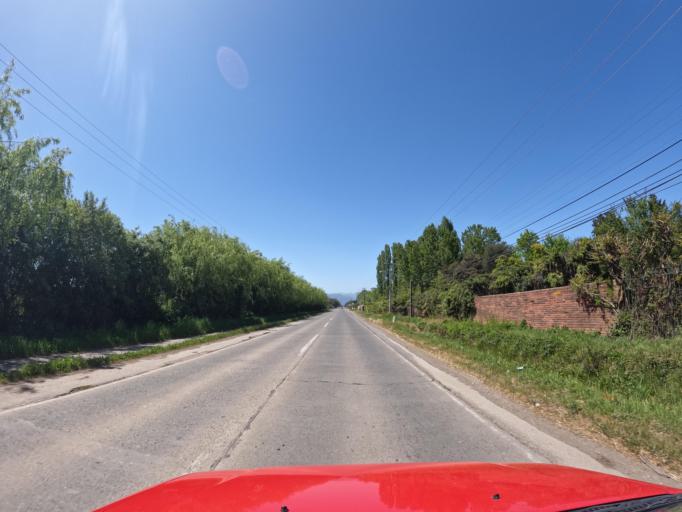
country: CL
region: Maule
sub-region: Provincia de Linares
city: Linares
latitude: -35.8335
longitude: -71.5382
